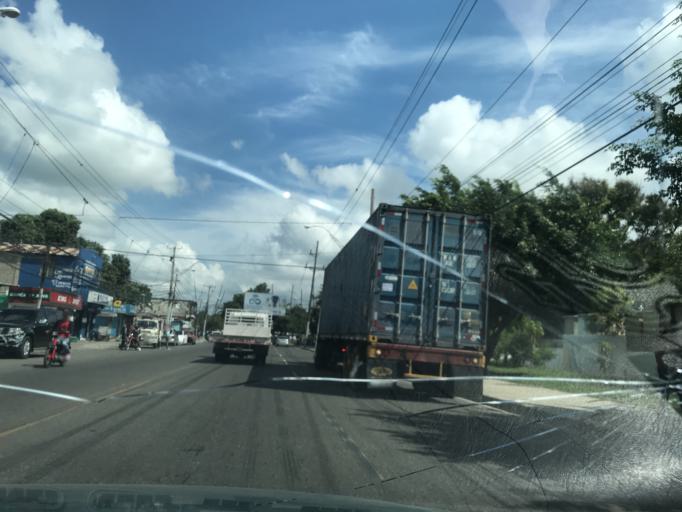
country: DO
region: Santiago
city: Palmar Arriba
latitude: 19.4916
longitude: -70.7364
